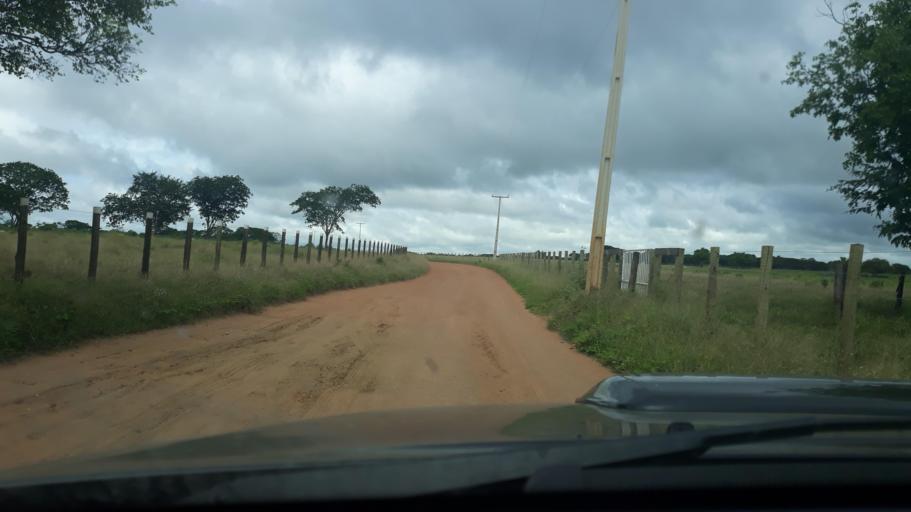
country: BR
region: Bahia
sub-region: Riacho De Santana
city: Riacho de Santana
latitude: -13.9008
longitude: -42.8877
